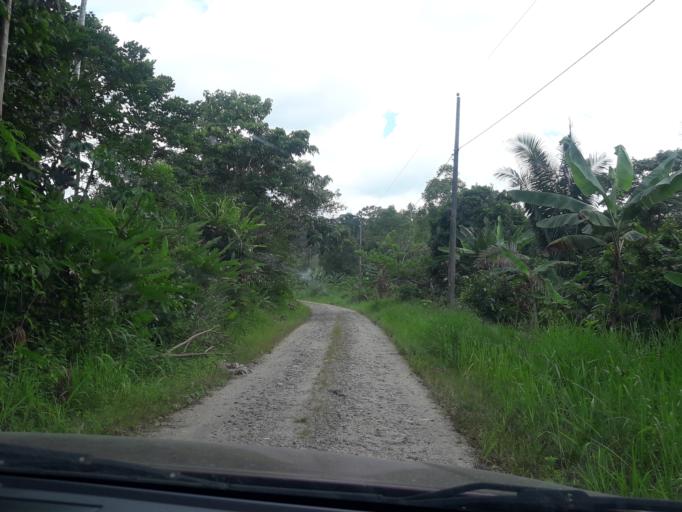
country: EC
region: Napo
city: Tena
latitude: -1.0964
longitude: -77.6783
